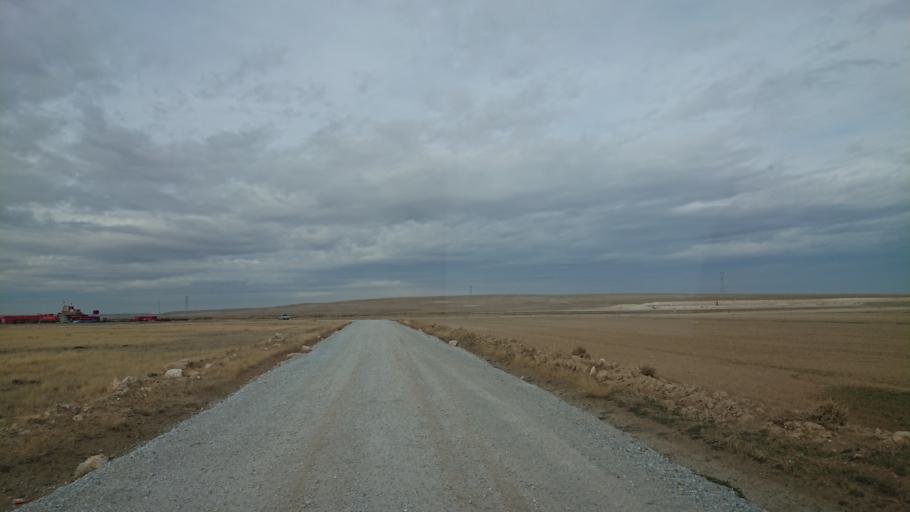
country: TR
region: Aksaray
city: Sultanhani
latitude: 38.1327
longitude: 33.5520
